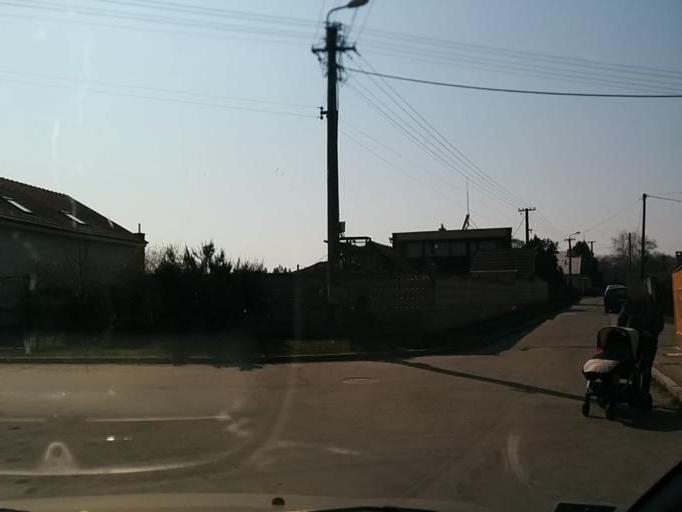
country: SK
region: Trnavsky
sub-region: Okres Galanta
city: Galanta
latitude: 48.2845
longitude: 17.7554
